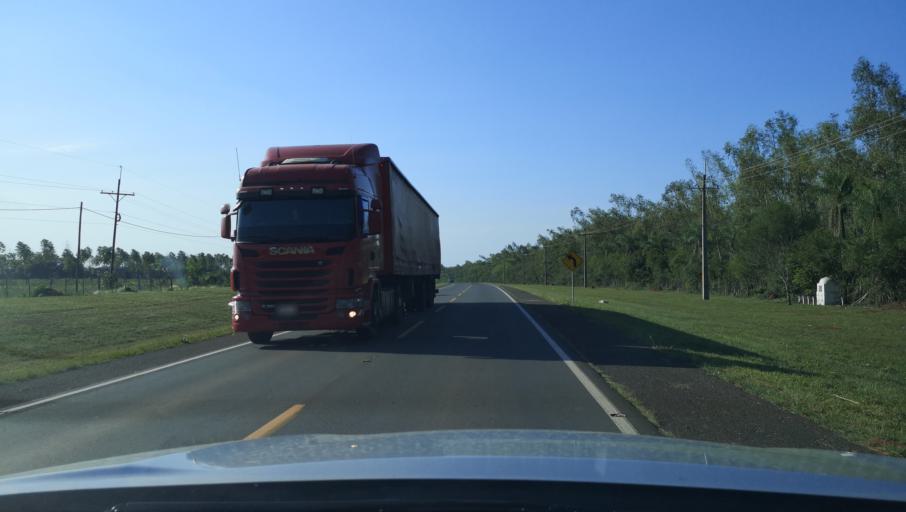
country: PY
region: Misiones
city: Santa Maria
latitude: -26.7625
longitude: -57.0332
